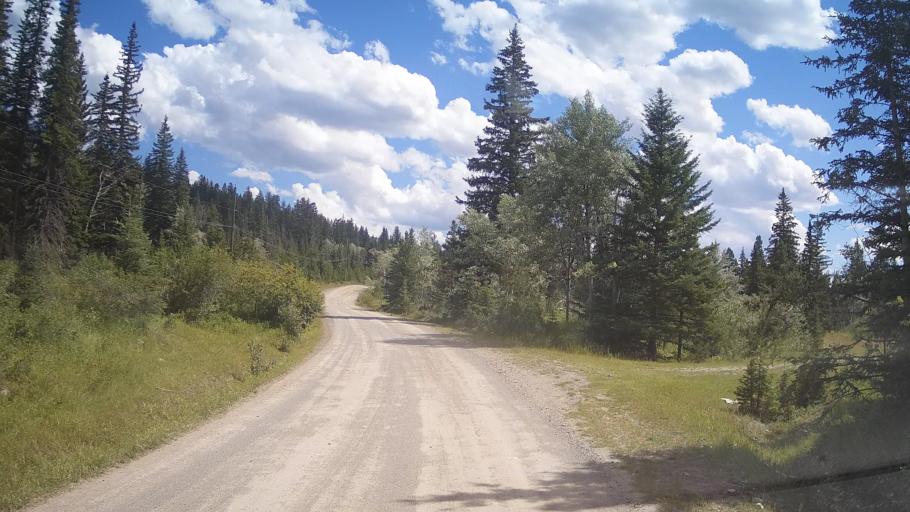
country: CA
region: British Columbia
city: Lillooet
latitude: 51.2924
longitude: -121.9787
